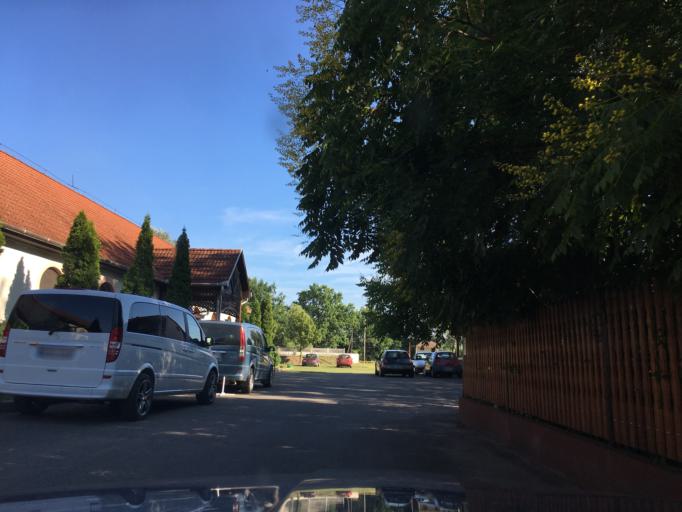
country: HU
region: Hajdu-Bihar
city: Hajdusamson
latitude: 47.6331
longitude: 21.8305
